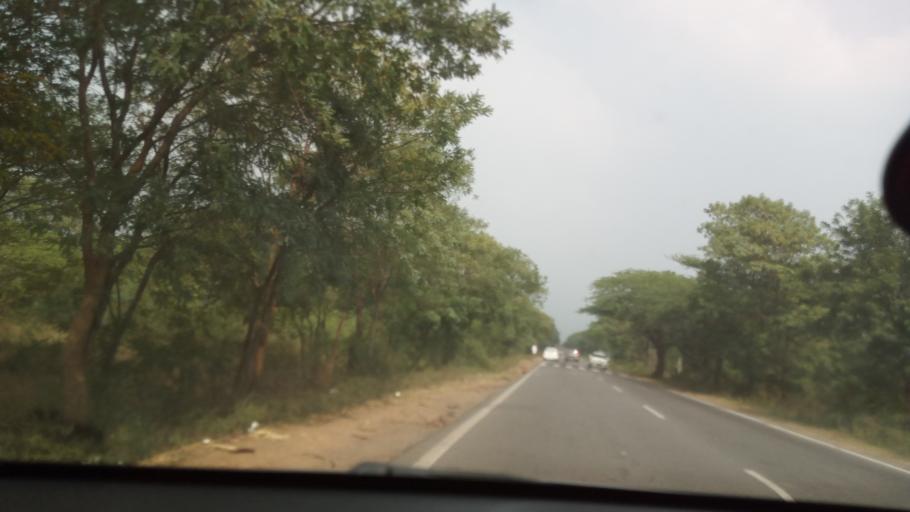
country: IN
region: Tamil Nadu
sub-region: Erode
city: Sathyamangalam
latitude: 11.5575
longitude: 77.1371
